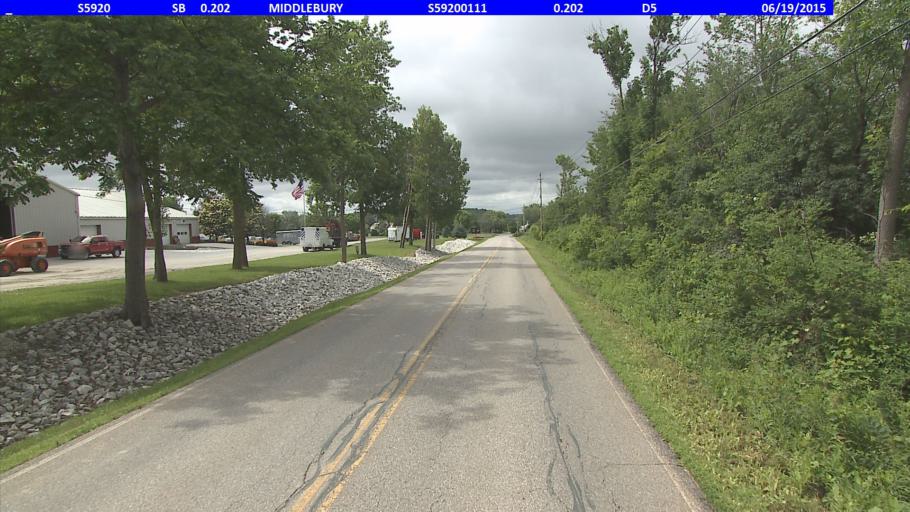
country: US
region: Vermont
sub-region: Addison County
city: Middlebury (village)
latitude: 43.9911
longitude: -73.1349
